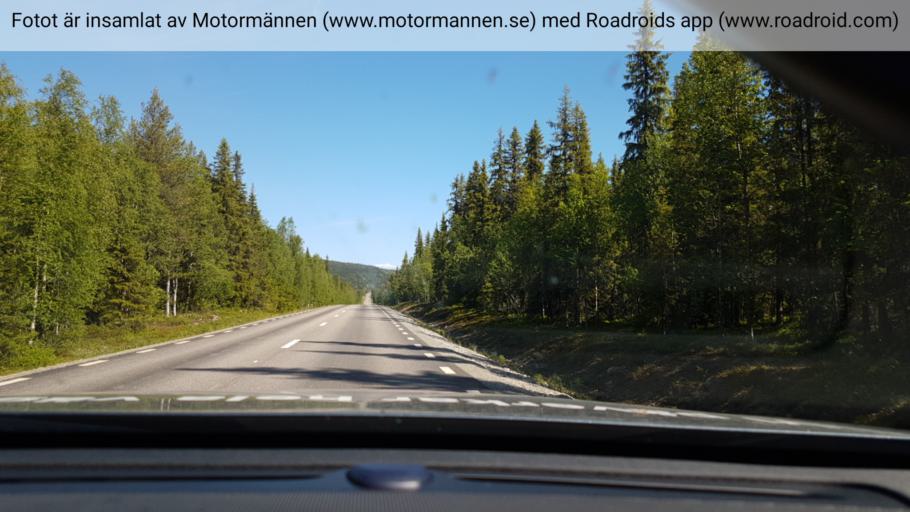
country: SE
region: Vaesterbotten
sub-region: Asele Kommun
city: Insjon
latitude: 64.7233
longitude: 17.6178
